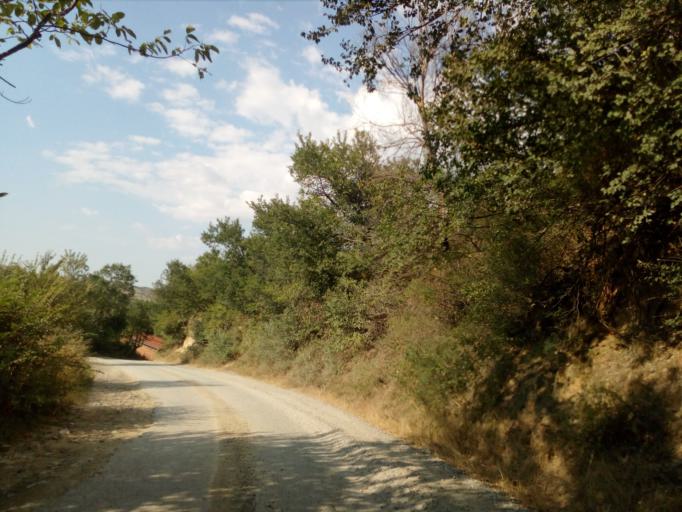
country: MK
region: Veles
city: Veles
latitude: 41.7359
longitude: 21.7893
